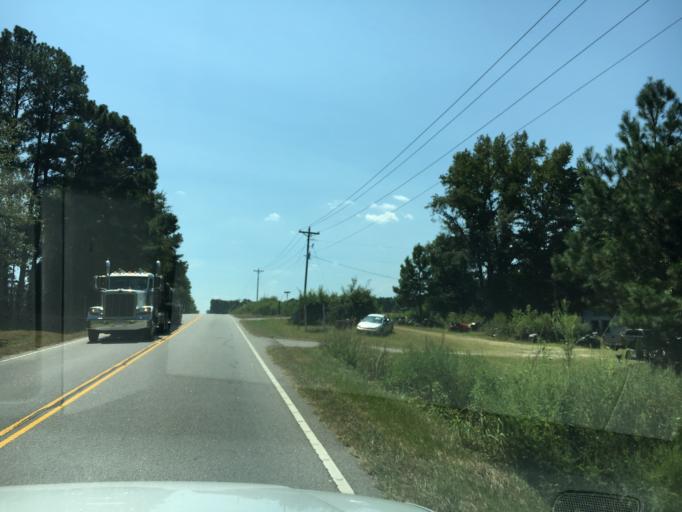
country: US
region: South Carolina
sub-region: Saluda County
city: Saluda
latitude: 33.9050
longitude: -81.7020
